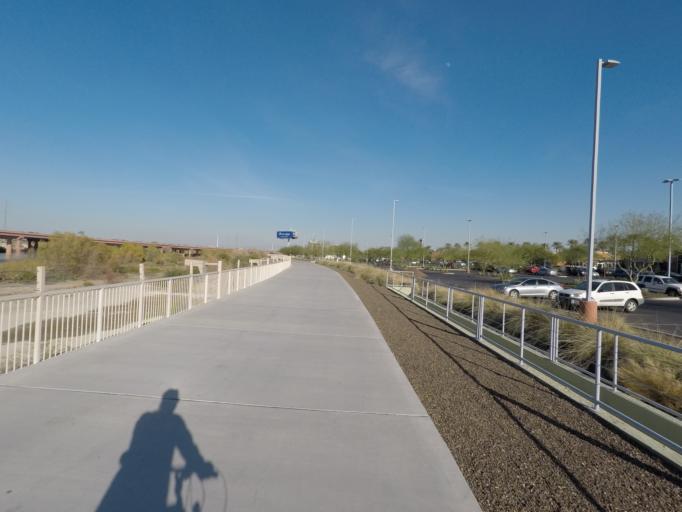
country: US
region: Arizona
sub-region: Maricopa County
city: Tempe
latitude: 33.4333
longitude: -111.9084
